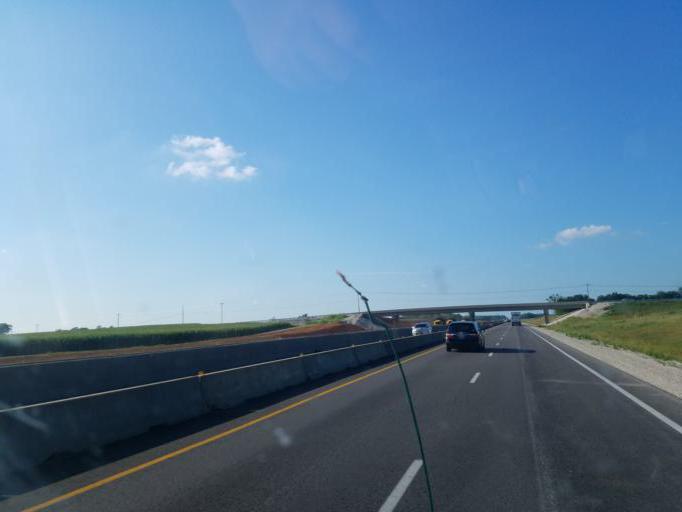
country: US
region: Kentucky
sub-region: Hardin County
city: Elizabethtown
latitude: 37.5715
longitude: -85.8738
